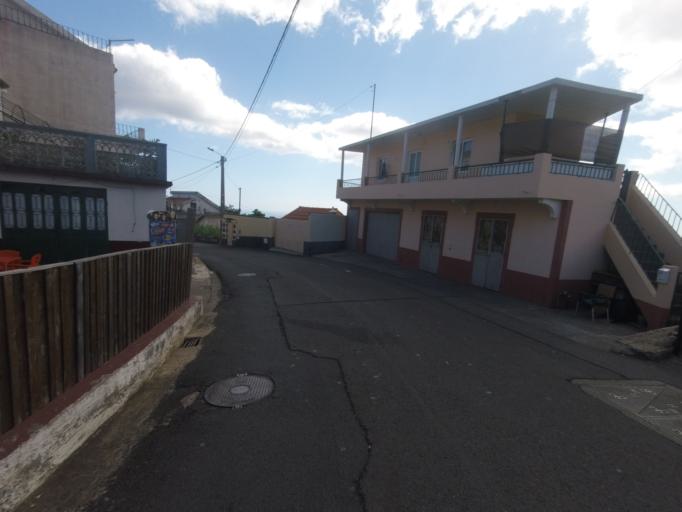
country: PT
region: Madeira
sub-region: Ribeira Brava
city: Campanario
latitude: 32.6741
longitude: -17.0527
